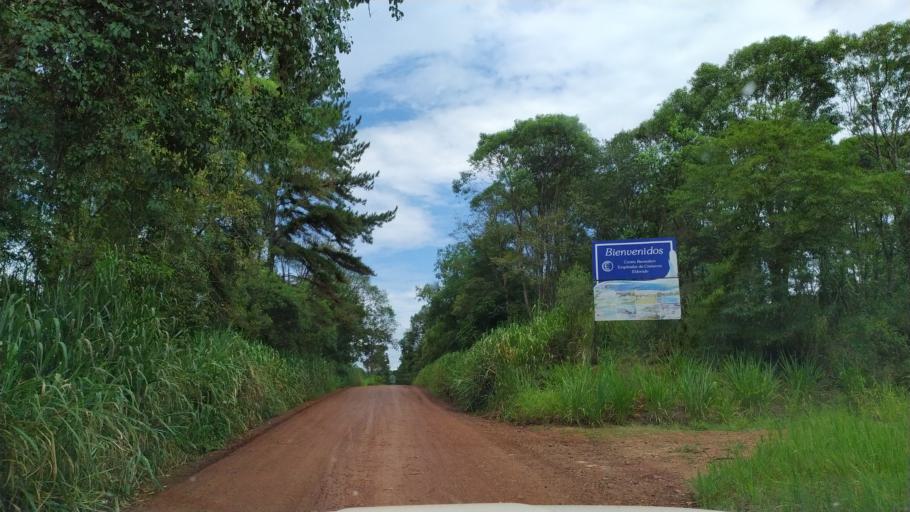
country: AR
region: Misiones
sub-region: Departamento de Eldorado
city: Eldorado
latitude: -26.4344
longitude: -54.6045
